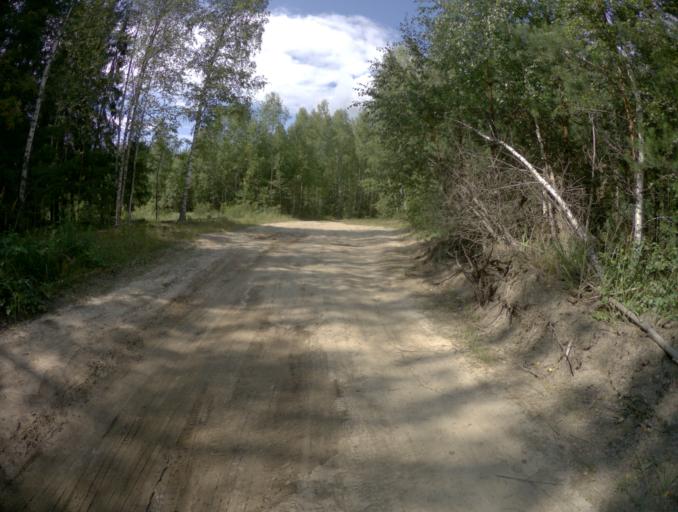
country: RU
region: Vladimir
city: Raduzhnyy
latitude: 55.9674
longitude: 40.2300
